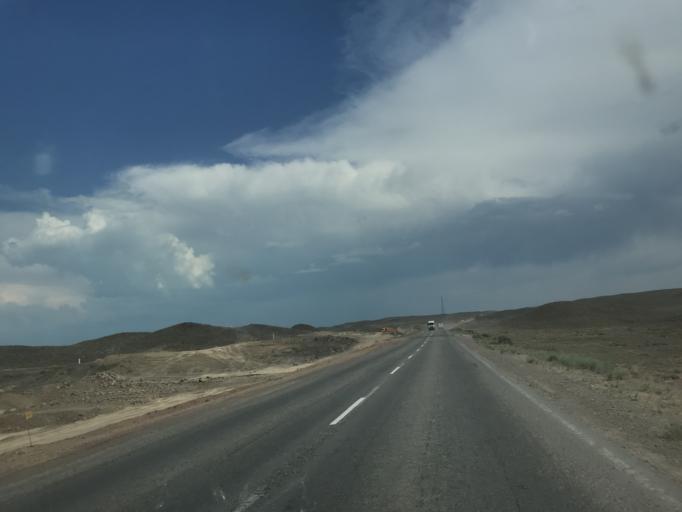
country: KZ
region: Zhambyl
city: Mynaral
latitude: 45.3403
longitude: 73.7077
